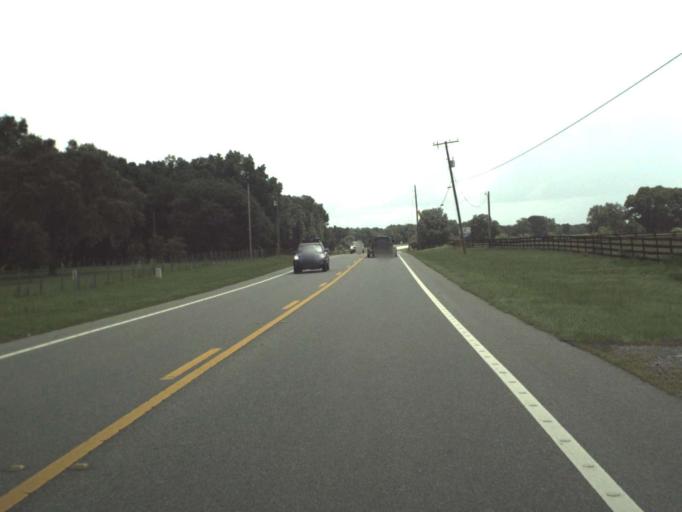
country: US
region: Florida
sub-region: Sumter County
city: Lake Panasoffkee
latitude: 28.7211
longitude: -82.0878
